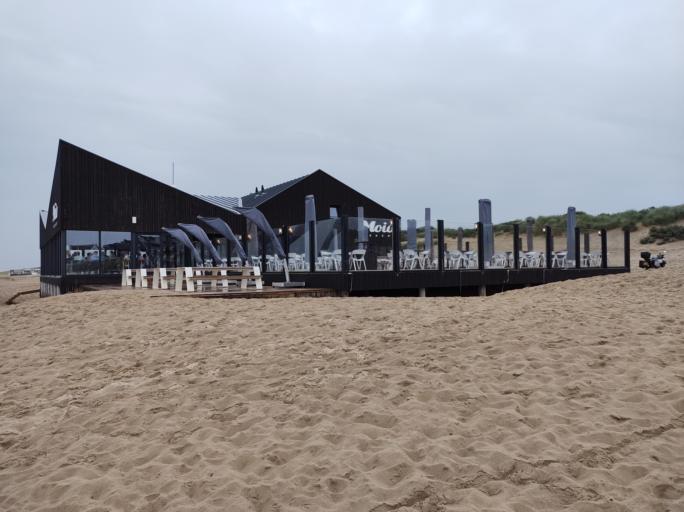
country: NL
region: Zeeland
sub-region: Gemeente Sluis
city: Sluis
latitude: 51.3838
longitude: 3.4047
